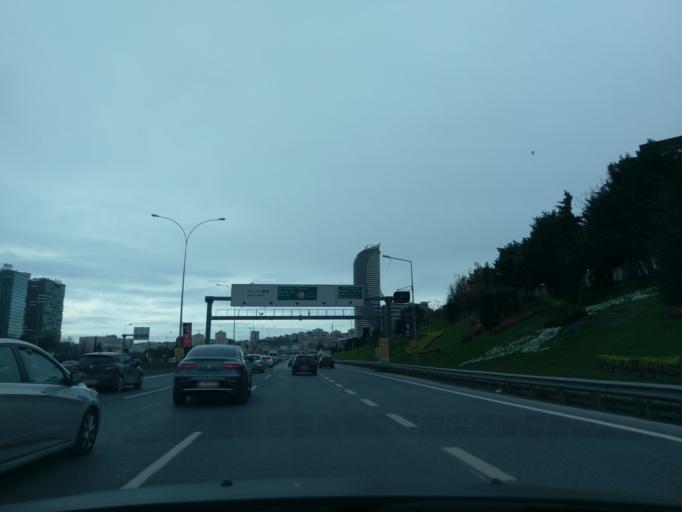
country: TR
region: Istanbul
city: UEskuedar
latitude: 40.9963
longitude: 29.0636
